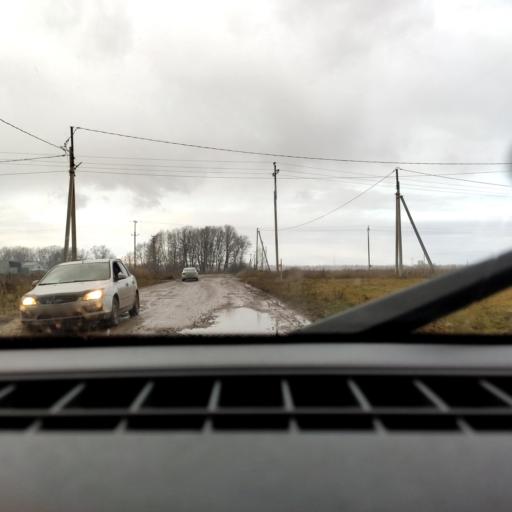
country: RU
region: Bashkortostan
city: Iglino
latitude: 54.7376
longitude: 56.3254
